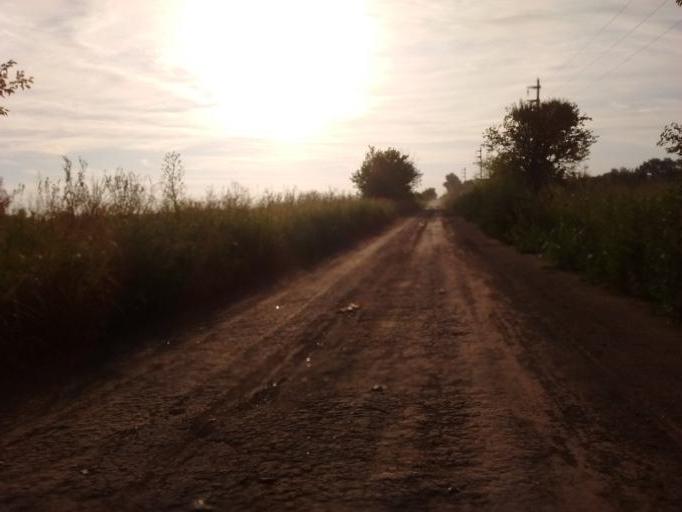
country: AR
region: Santa Fe
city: Funes
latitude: -32.9308
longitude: -60.8596
